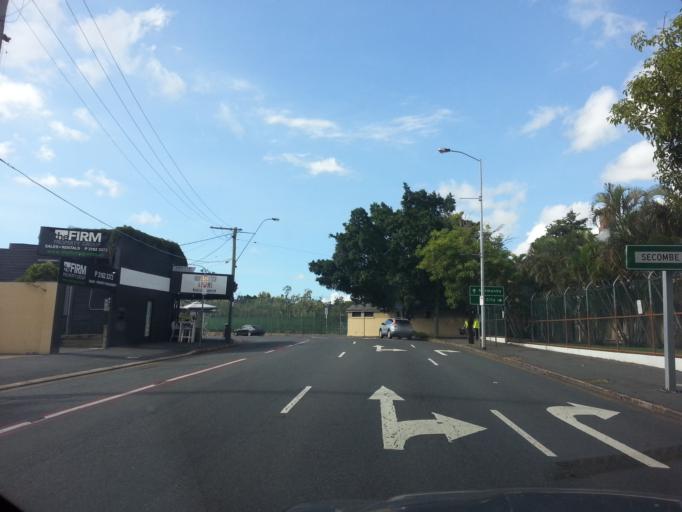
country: AU
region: Queensland
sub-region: Brisbane
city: Spring Hill
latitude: -27.4643
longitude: 153.0141
